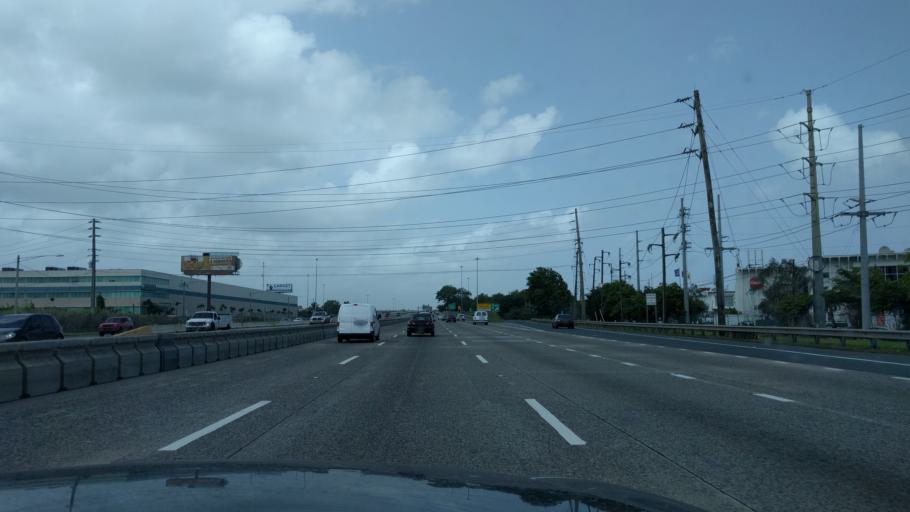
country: PR
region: Catano
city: Catano
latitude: 18.4229
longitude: -66.1364
